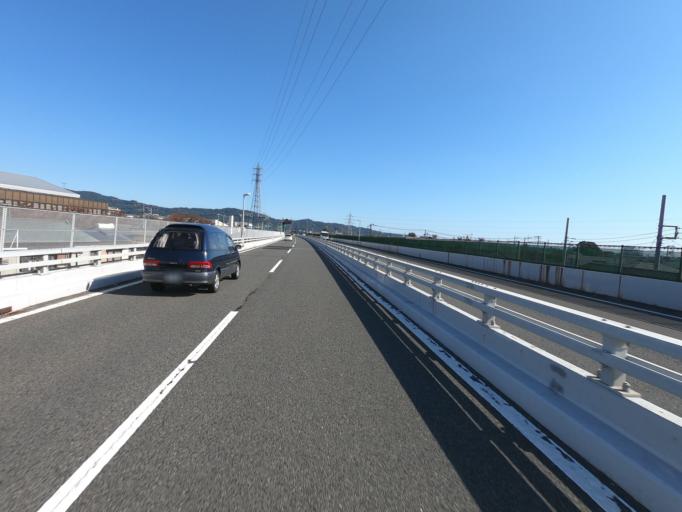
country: JP
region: Kanagawa
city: Odawara
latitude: 35.2841
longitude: 139.1647
